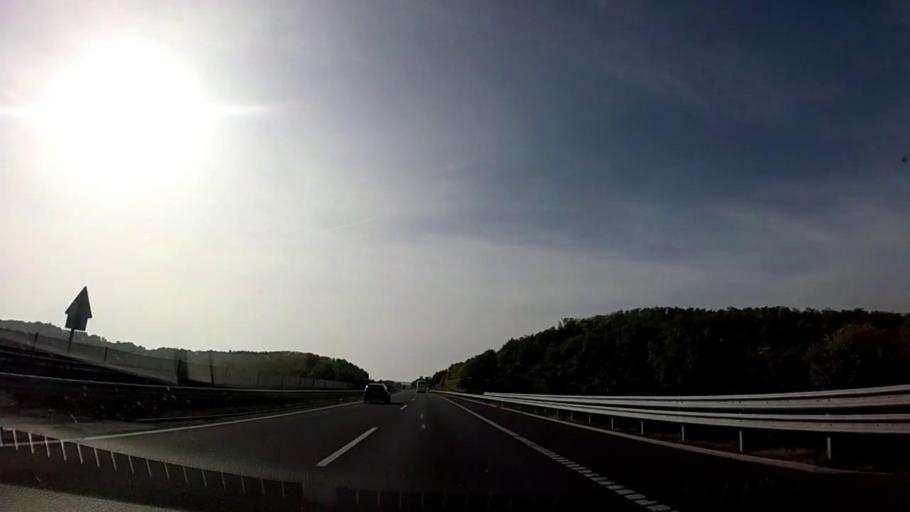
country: HU
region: Somogy
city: Zamardi
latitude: 46.8460
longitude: 17.9537
